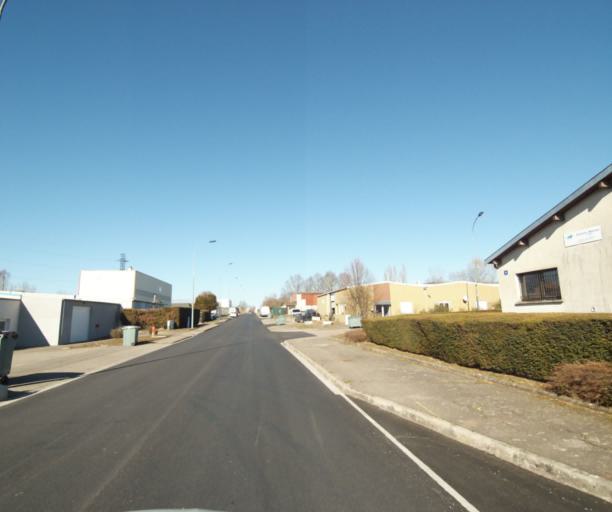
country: FR
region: Lorraine
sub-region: Departement de Meurthe-et-Moselle
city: Heillecourt
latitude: 48.6500
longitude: 6.2095
